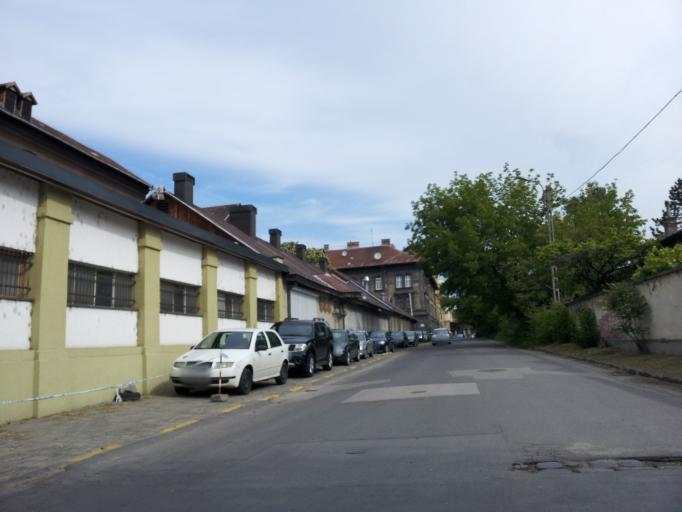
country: HU
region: Budapest
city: Budapest VII. keruelet
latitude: 47.4976
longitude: 19.0853
